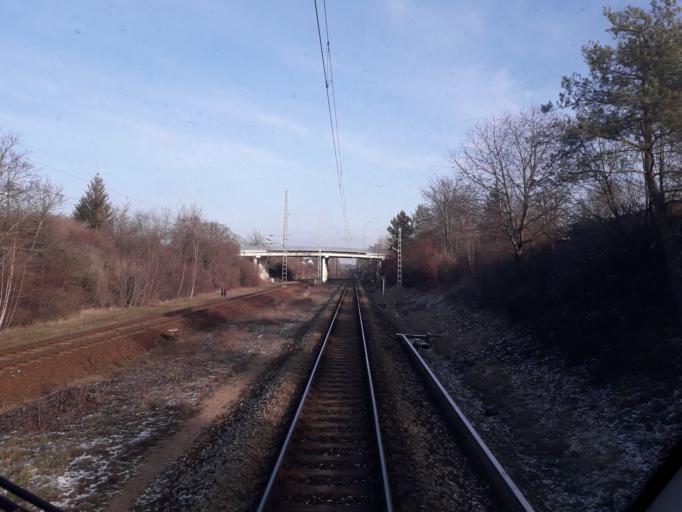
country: DE
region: Berlin
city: Altglienicke
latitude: 52.3996
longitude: 13.5304
